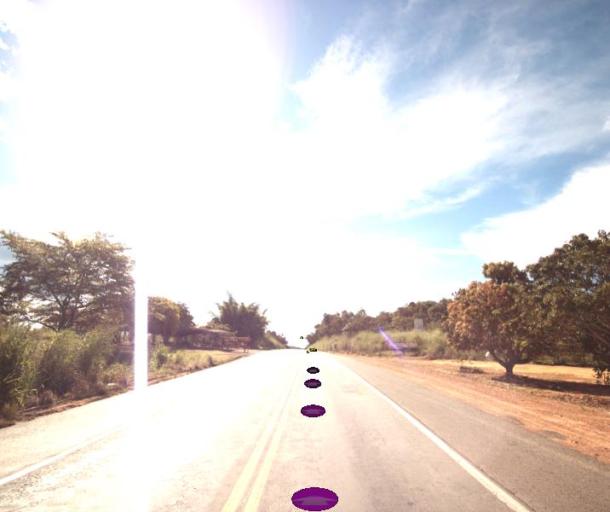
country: BR
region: Goias
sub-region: Uruana
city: Uruana
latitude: -15.5121
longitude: -49.4733
